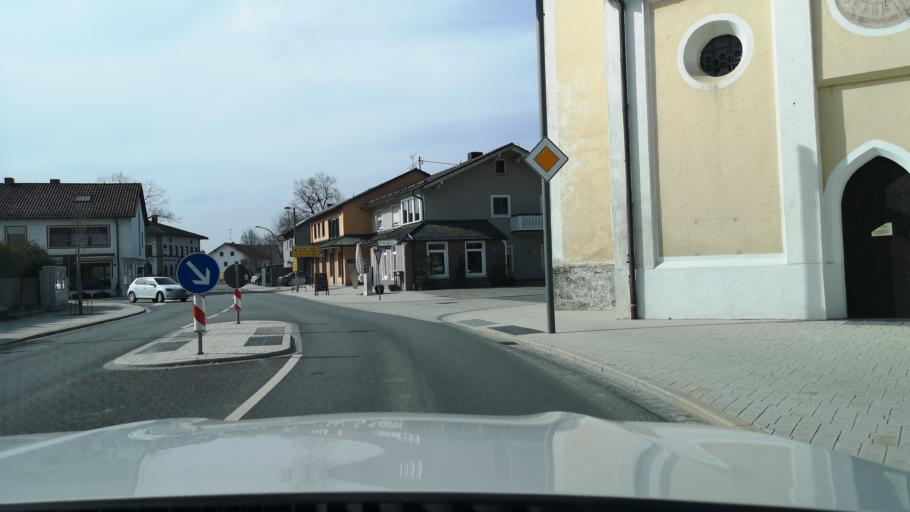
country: DE
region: Bavaria
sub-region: Upper Bavaria
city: Hohenlinden
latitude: 48.1572
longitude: 11.9972
